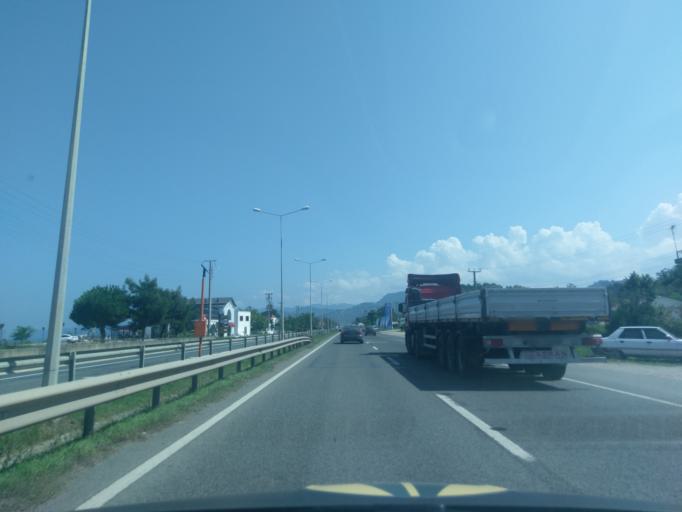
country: TR
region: Ordu
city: Fatsa
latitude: 41.0221
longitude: 37.5440
